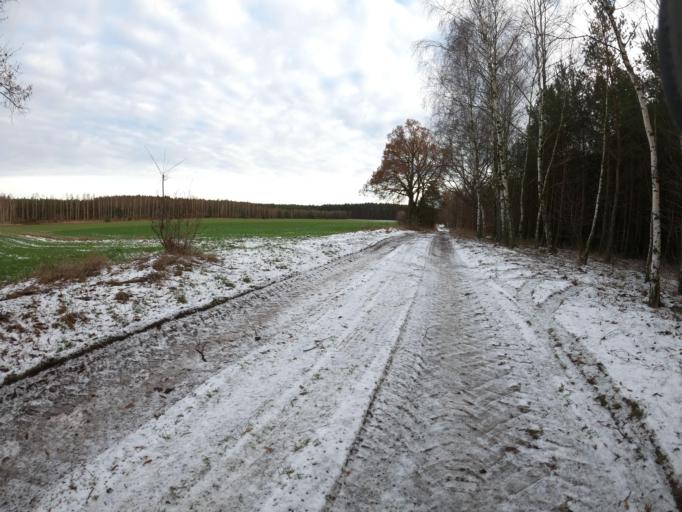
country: PL
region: Lubusz
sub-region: Powiat slubicki
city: Cybinka
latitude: 52.1996
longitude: 14.8606
